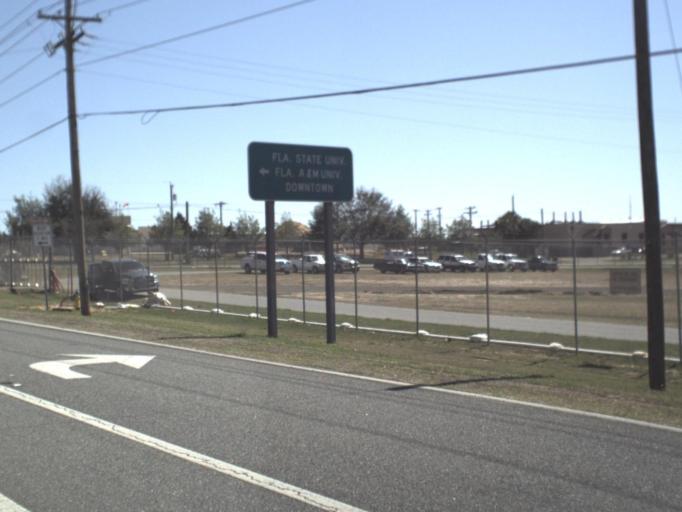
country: US
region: Florida
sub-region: Leon County
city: Tallahassee
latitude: 30.3944
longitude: -84.3227
